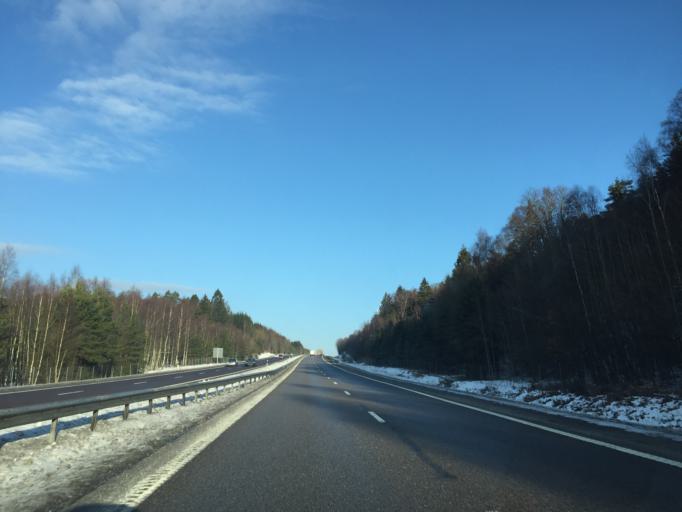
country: SE
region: Vaestra Goetaland
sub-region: Stenungsunds Kommun
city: Stenungsund
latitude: 58.0758
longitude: 11.8892
